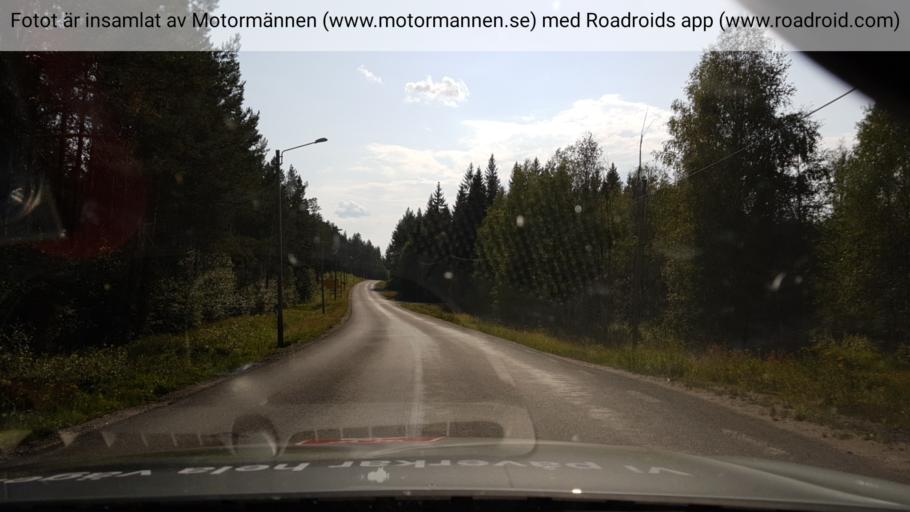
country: SE
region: Jaemtland
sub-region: Braecke Kommun
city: Braecke
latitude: 62.3968
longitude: 15.1483
